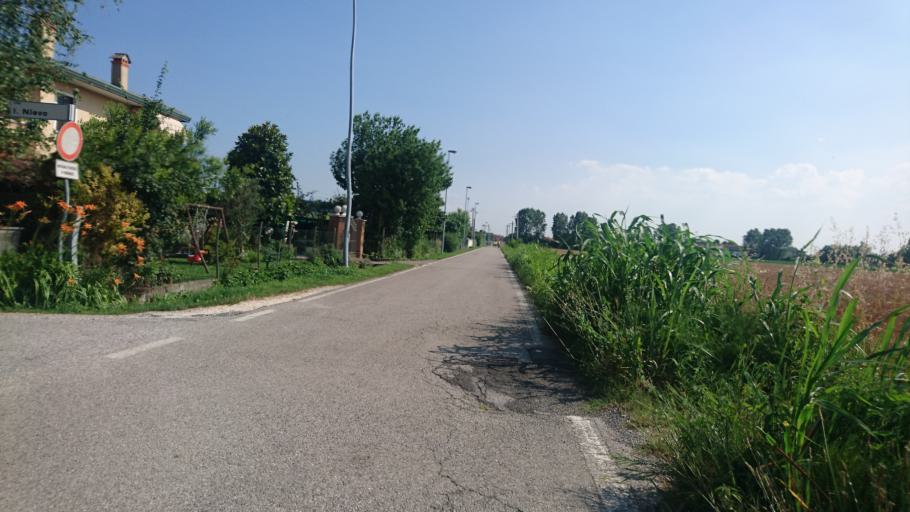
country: IT
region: Veneto
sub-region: Provincia di Venezia
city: Fornase
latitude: 45.4387
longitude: 12.1939
